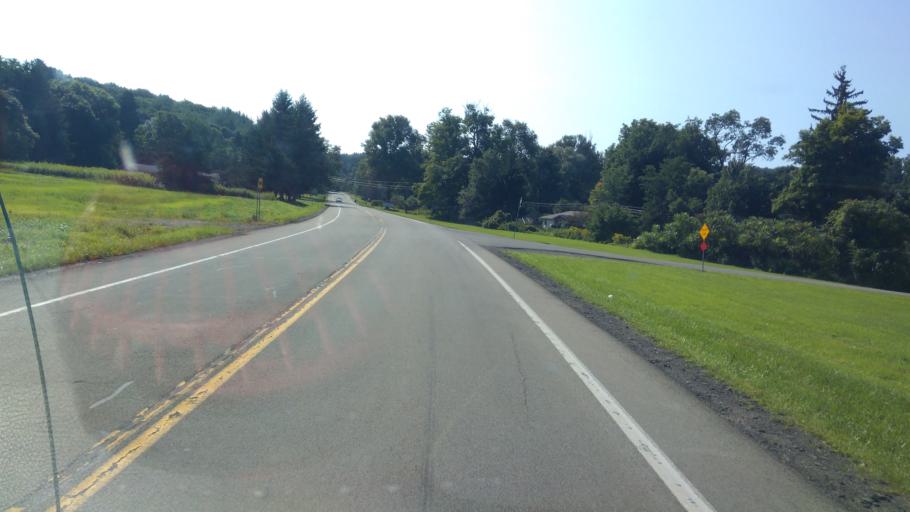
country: US
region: New York
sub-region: Allegany County
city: Cuba
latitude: 42.2011
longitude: -78.2744
